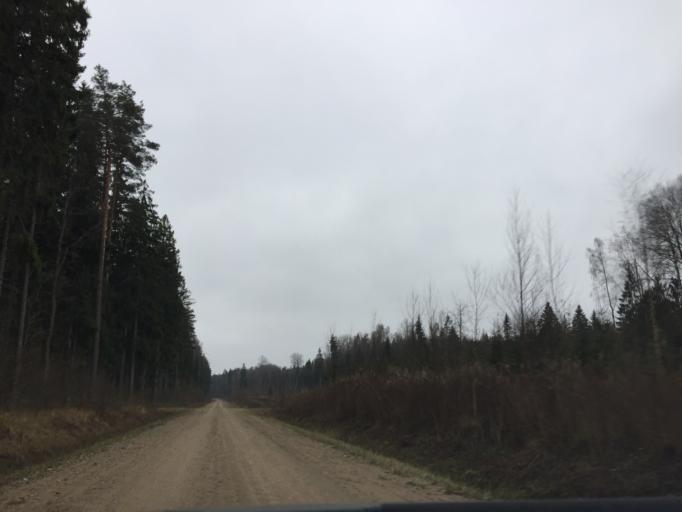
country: LV
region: Limbazu Rajons
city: Limbazi
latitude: 57.4695
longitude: 24.7553
